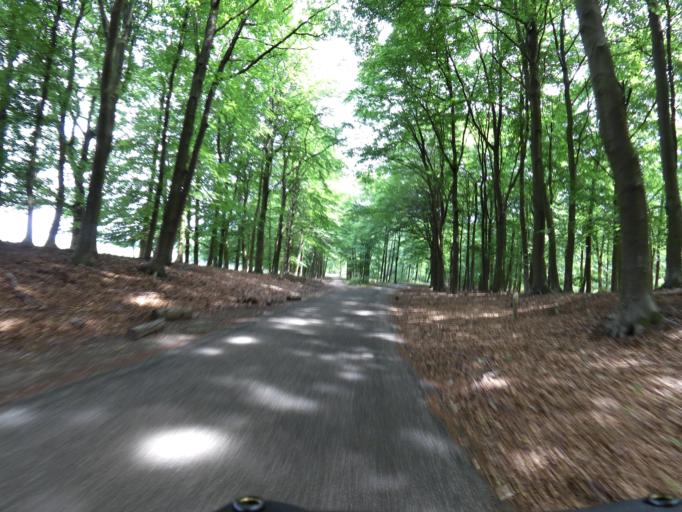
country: NL
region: Gelderland
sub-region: Gemeente Apeldoorn
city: Loenen
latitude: 52.0884
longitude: 5.9593
